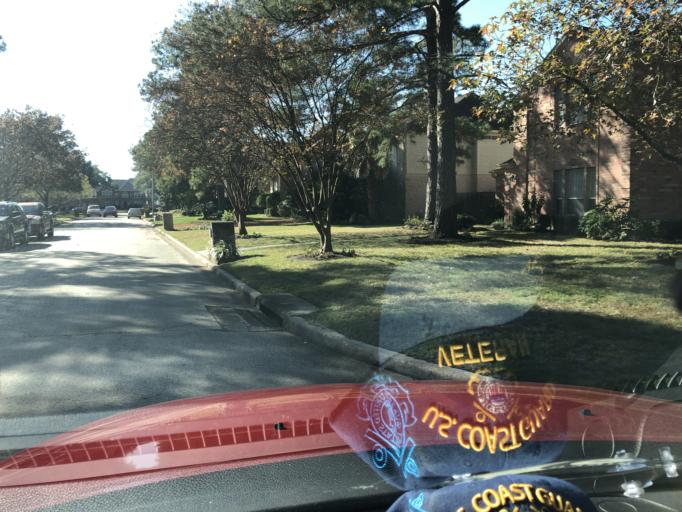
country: US
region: Texas
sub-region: Harris County
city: Tomball
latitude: 30.0339
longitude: -95.5477
